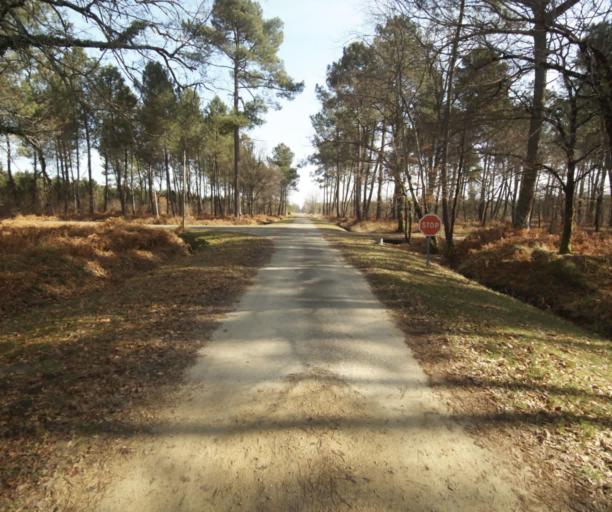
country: FR
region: Aquitaine
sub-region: Departement des Landes
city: Roquefort
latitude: 44.2187
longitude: -0.2202
